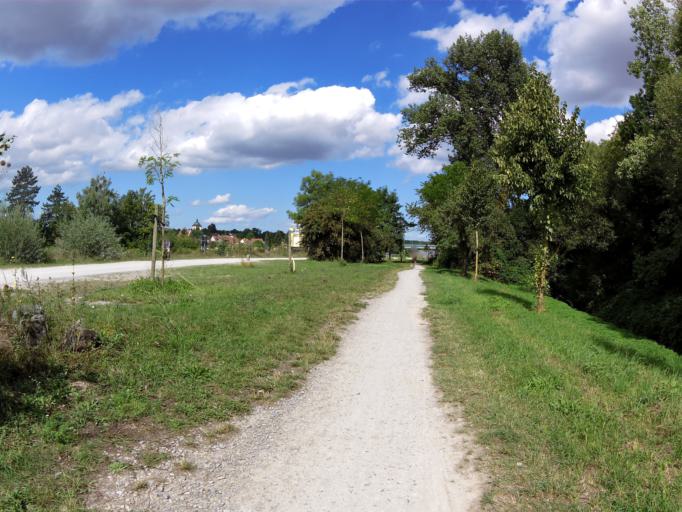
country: DE
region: Bavaria
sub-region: Regierungsbezirk Unterfranken
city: Volkach
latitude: 49.8608
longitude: 10.2230
